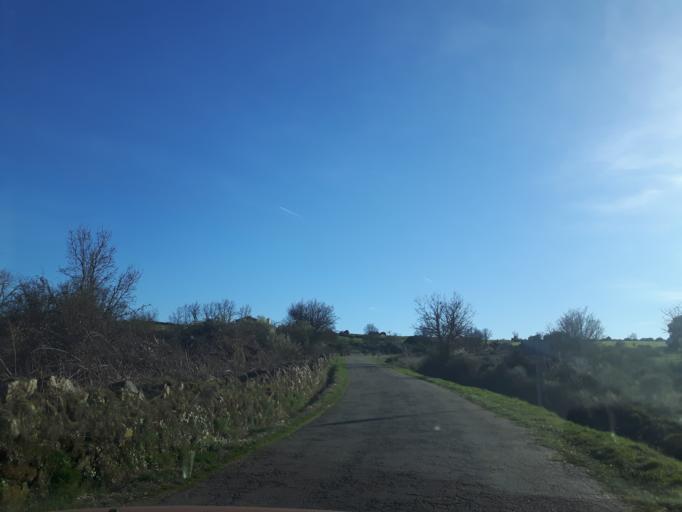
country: ES
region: Castille and Leon
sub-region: Provincia de Salamanca
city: Saldeana
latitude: 40.9856
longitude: -6.6284
